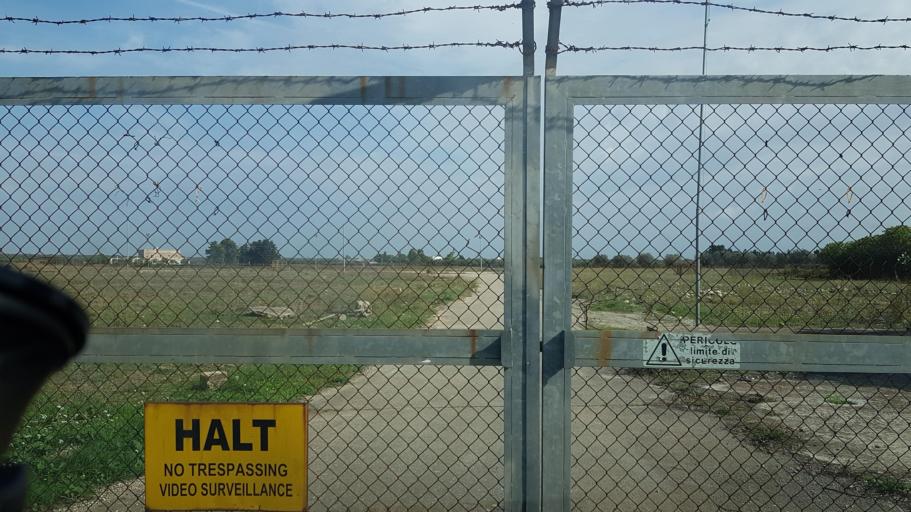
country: IT
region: Apulia
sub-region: Provincia di Brindisi
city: San Pancrazio Salentino
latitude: 40.4322
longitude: 17.8599
